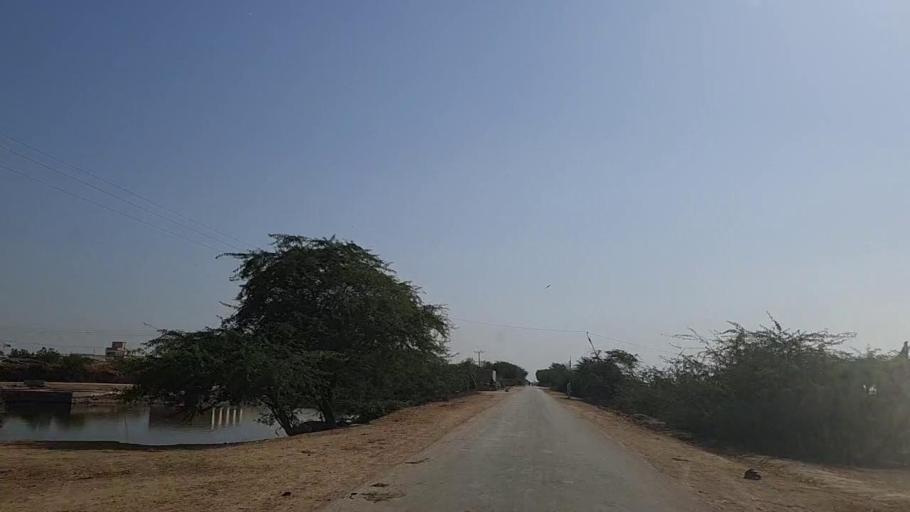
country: PK
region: Sindh
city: Mirpur Batoro
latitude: 24.6408
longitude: 68.2908
